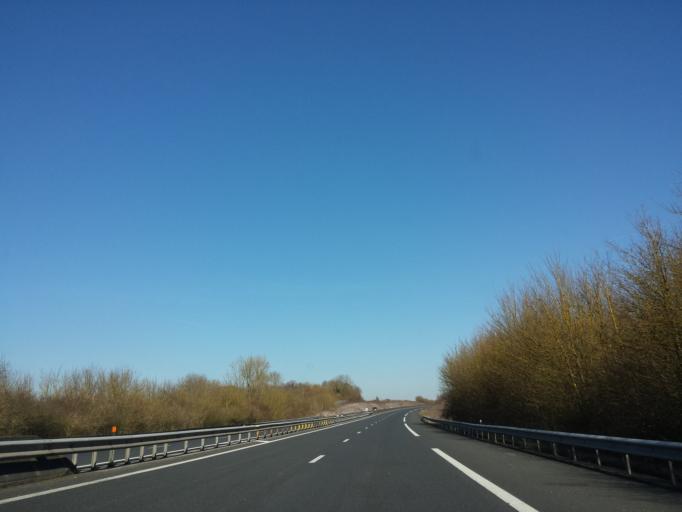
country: FR
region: Picardie
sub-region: Departement de l'Oise
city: Tille
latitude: 49.5299
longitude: 2.1845
